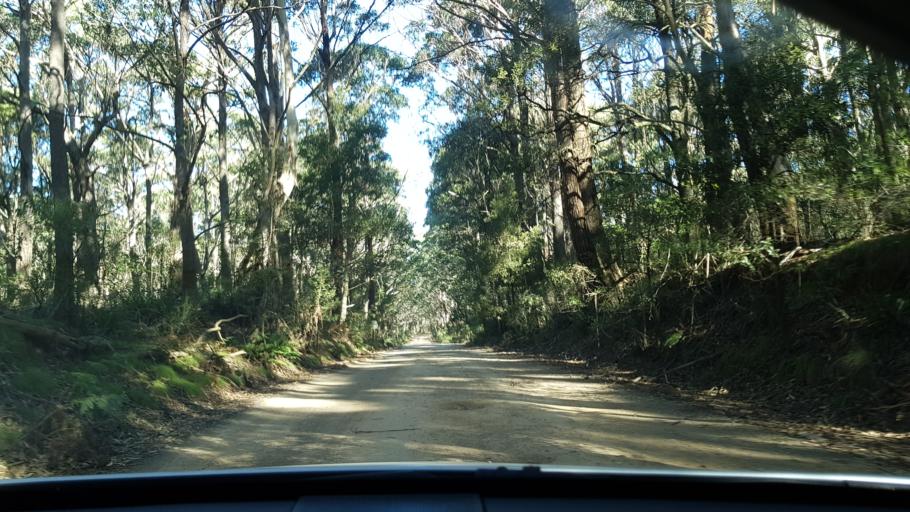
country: AU
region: New South Wales
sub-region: Oberon
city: Oberon
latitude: -33.8685
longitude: 150.0471
